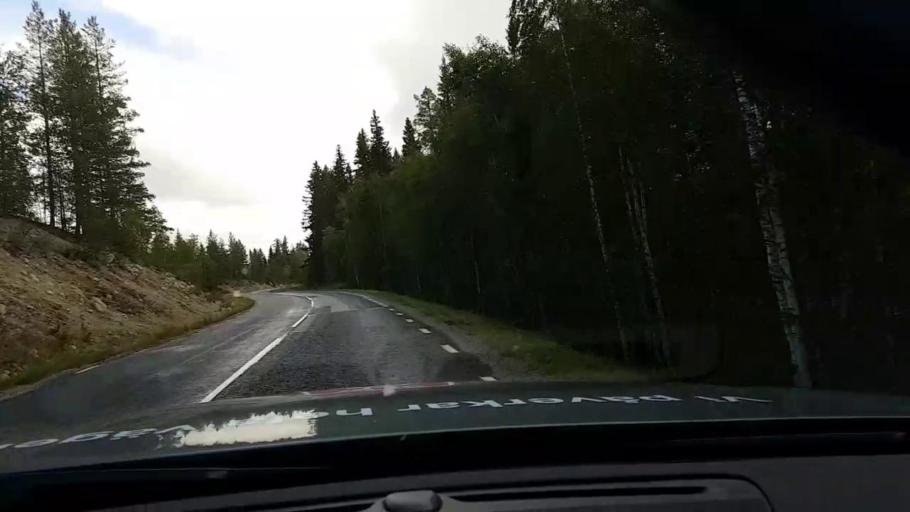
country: SE
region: Vaesterbotten
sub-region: Asele Kommun
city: Asele
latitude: 63.8344
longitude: 17.4453
